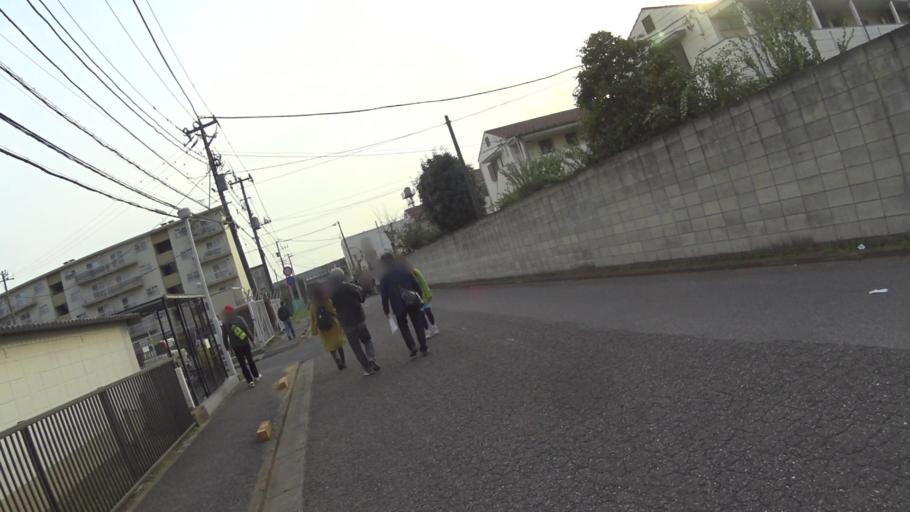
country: JP
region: Chiba
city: Funabashi
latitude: 35.6834
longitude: 140.0011
